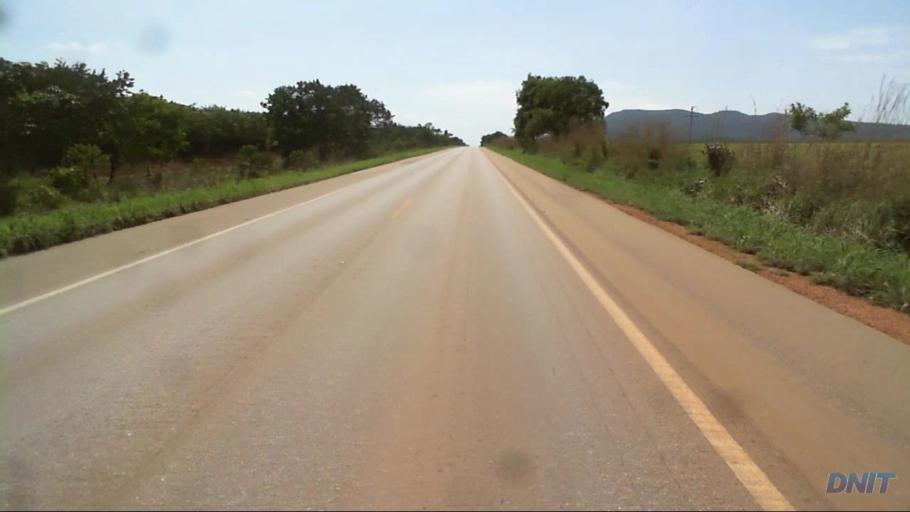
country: BR
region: Goias
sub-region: Barro Alto
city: Barro Alto
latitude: -15.1949
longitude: -48.7679
